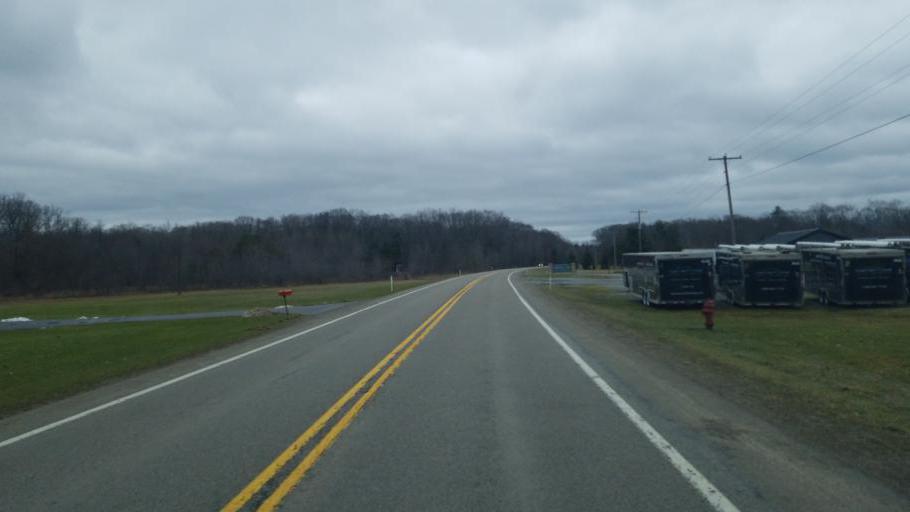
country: US
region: Pennsylvania
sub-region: Forest County
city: Marienville
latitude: 41.3998
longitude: -79.2552
